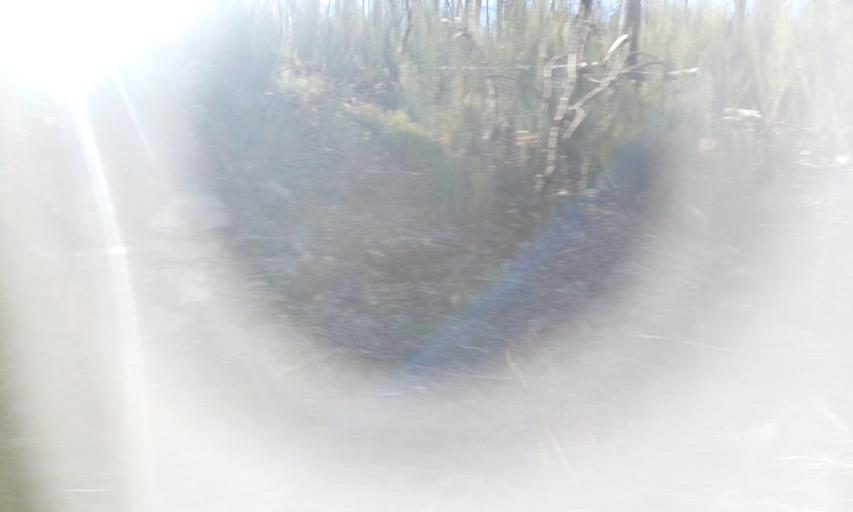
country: PT
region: Guarda
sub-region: Manteigas
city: Manteigas
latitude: 40.4891
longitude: -7.5387
